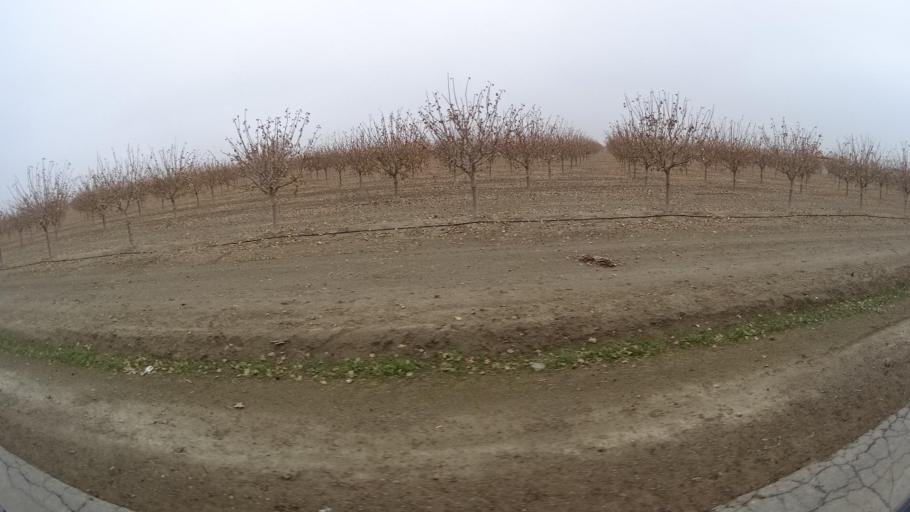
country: US
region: California
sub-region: Kern County
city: Wasco
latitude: 35.6853
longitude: -119.5086
